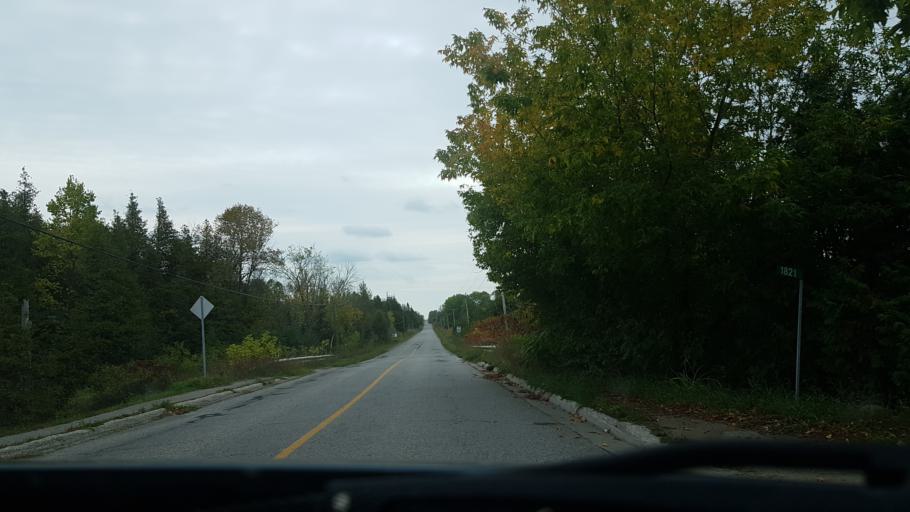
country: CA
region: Ontario
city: Omemee
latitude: 44.5945
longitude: -78.9389
